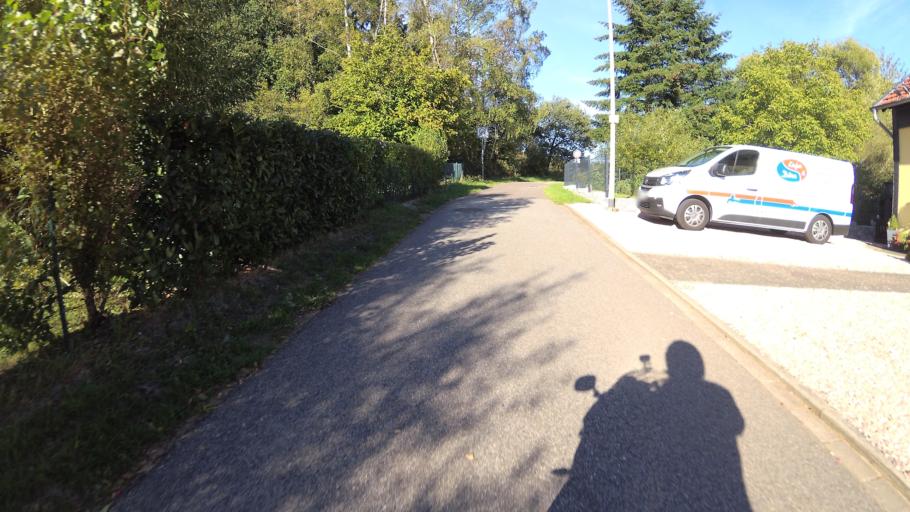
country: DE
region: Saarland
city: Eppelborn
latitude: 49.3563
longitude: 6.9838
